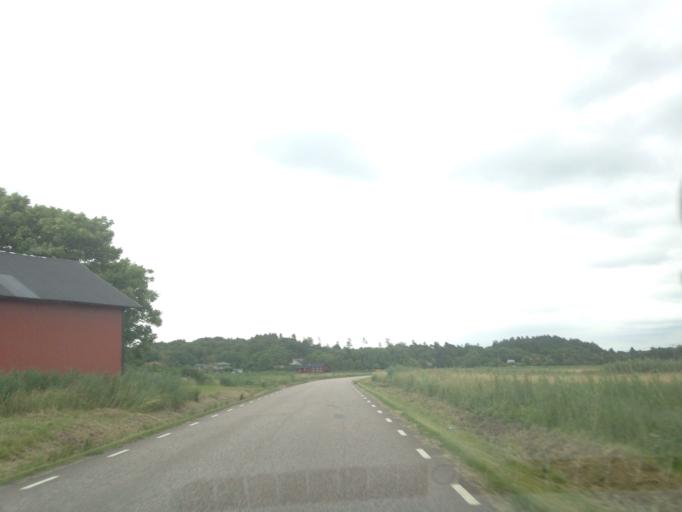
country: SE
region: Vaestra Goetaland
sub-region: Kungalvs Kommun
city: Kode
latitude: 57.8199
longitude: 11.8572
